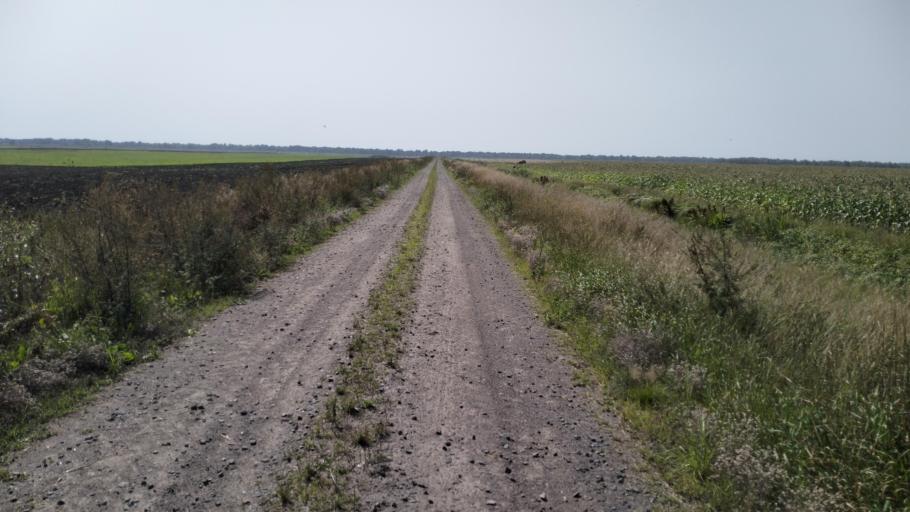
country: BY
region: Brest
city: Davyd-Haradok
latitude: 51.9857
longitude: 27.1639
